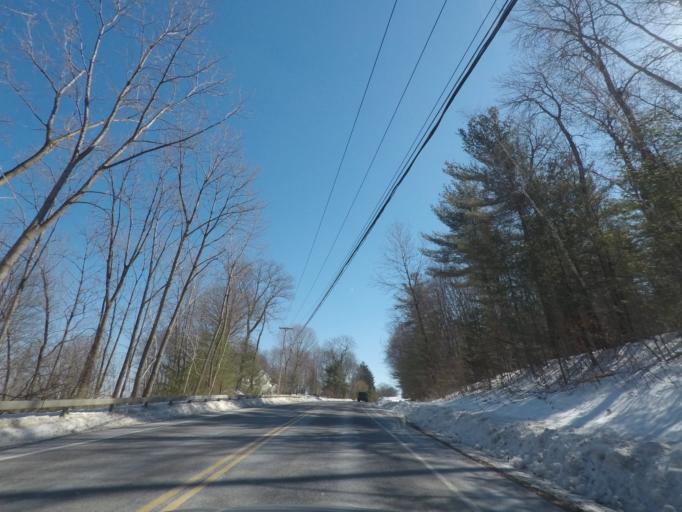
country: US
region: New York
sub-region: Saratoga County
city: Saratoga Springs
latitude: 43.0525
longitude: -73.7500
